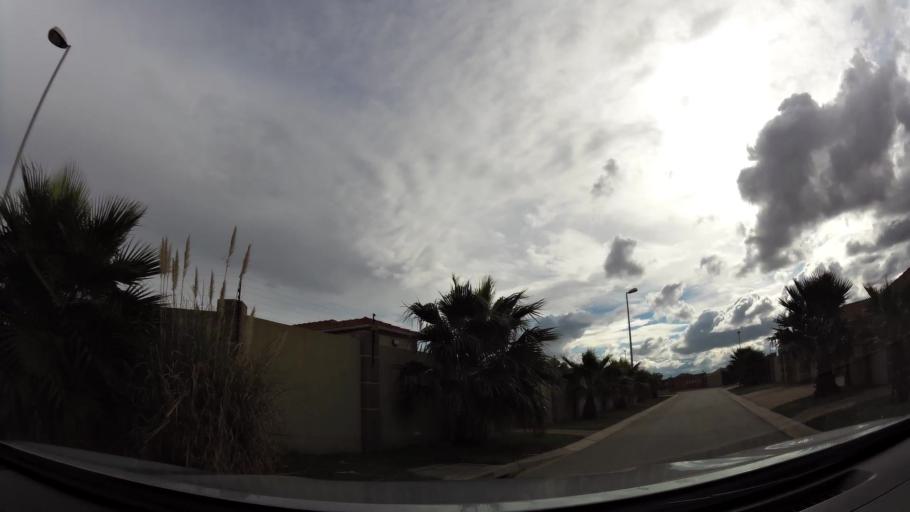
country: ZA
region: Eastern Cape
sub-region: Nelson Mandela Bay Metropolitan Municipality
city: Port Elizabeth
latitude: -33.9336
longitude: 25.5020
